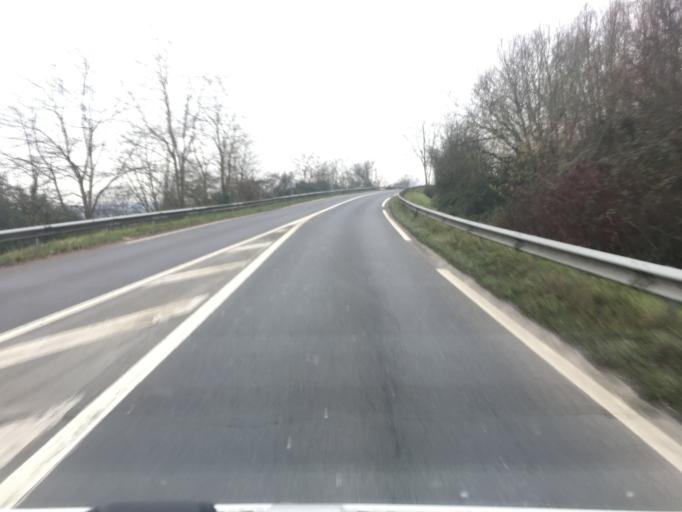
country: FR
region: Lower Normandy
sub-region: Departement du Calvados
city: Touques
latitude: 49.3331
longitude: 0.1116
